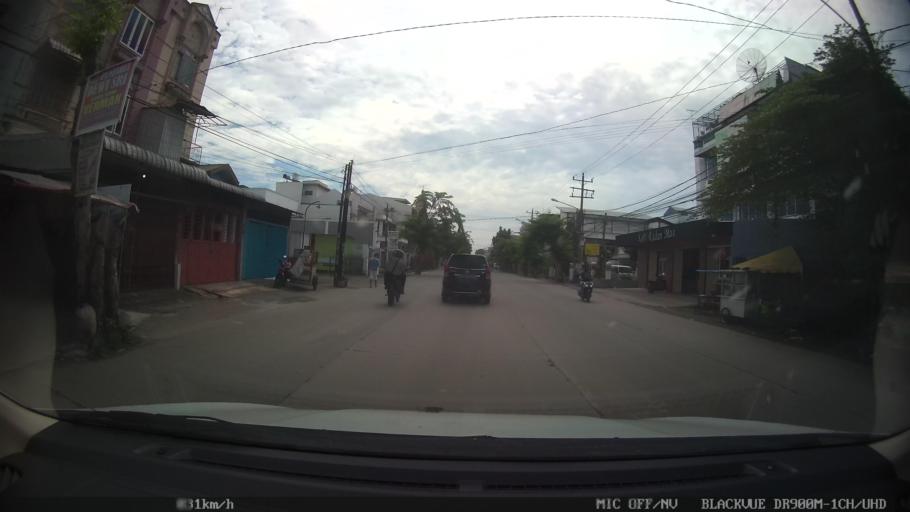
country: ID
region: North Sumatra
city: Medan
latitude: 3.6232
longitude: 98.6756
